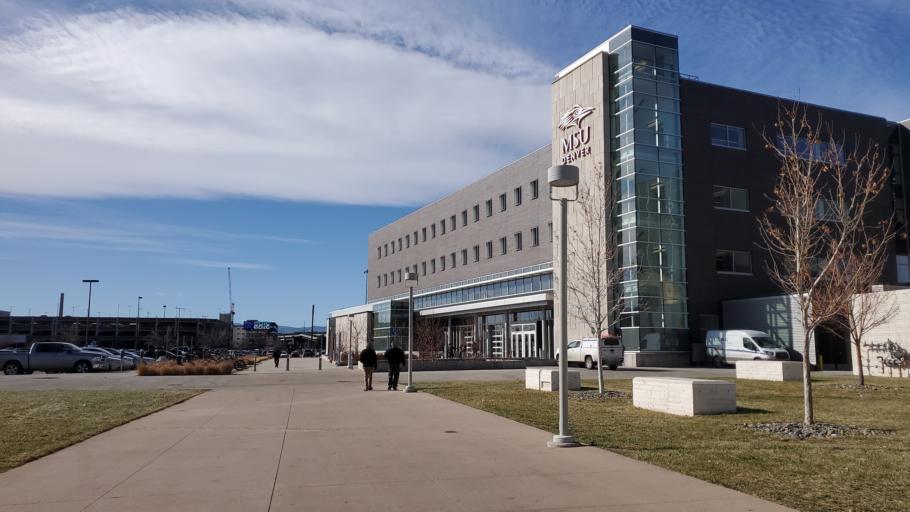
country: US
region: Colorado
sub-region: Denver County
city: Denver
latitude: 39.7452
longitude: -105.0077
